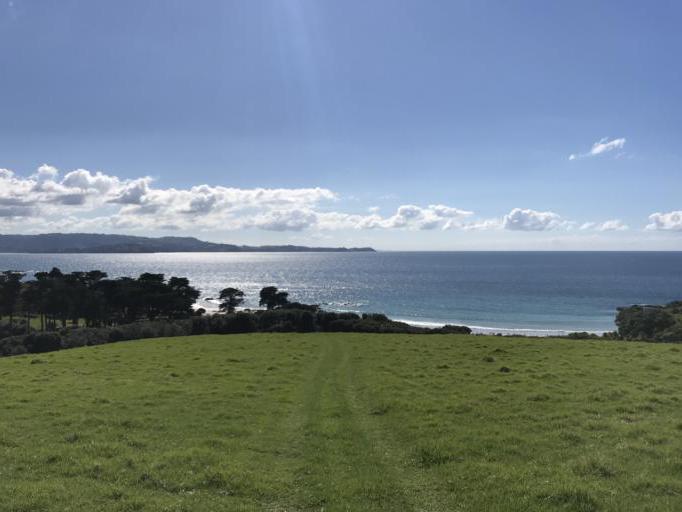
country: NZ
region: Auckland
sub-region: Auckland
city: Warkworth
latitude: -36.3710
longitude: 174.8354
